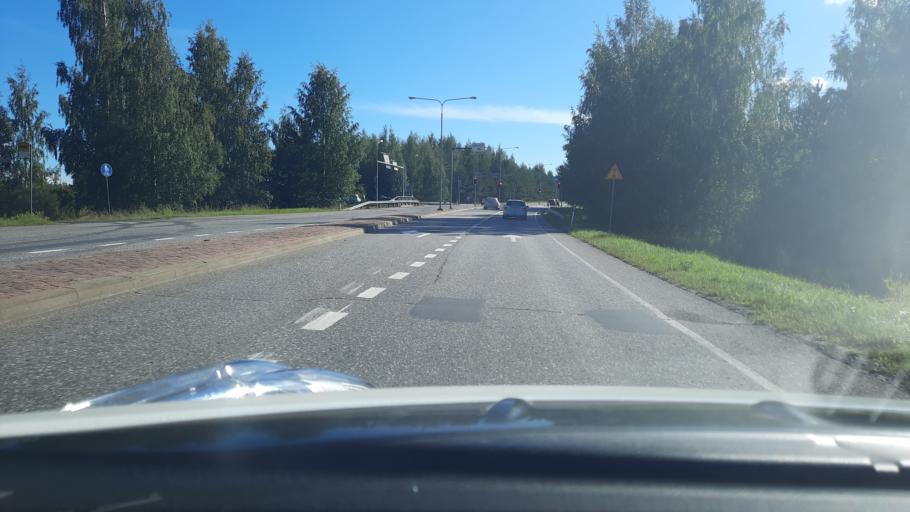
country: FI
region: North Karelia
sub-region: Joensuu
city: Joensuu
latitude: 62.6316
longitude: 29.7003
